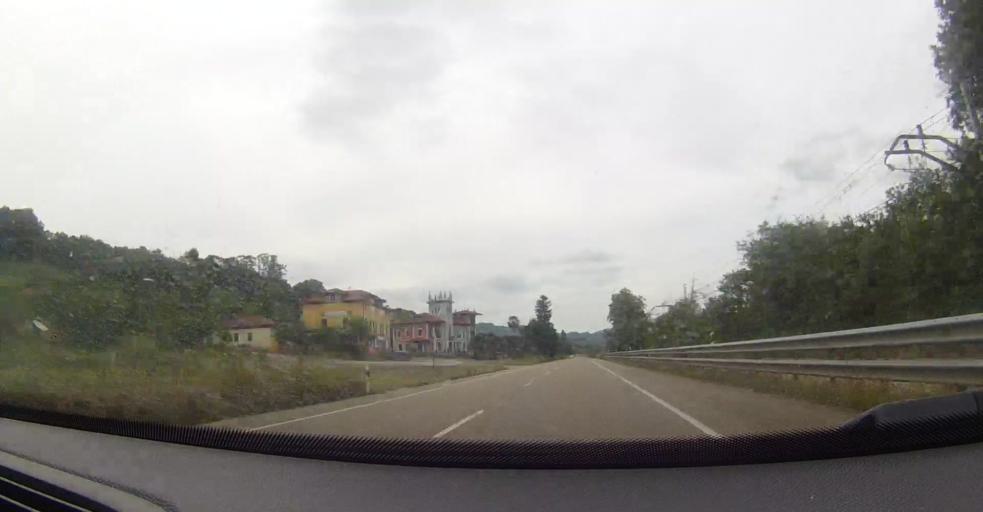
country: ES
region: Asturias
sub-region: Province of Asturias
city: Pilona
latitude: 43.3662
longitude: -5.2776
